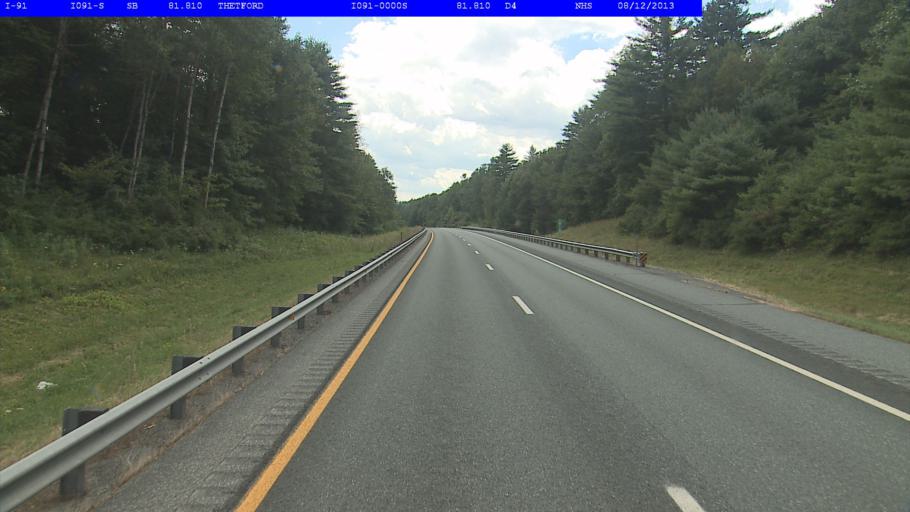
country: US
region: New Hampshire
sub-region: Grafton County
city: Lyme
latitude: 43.7803
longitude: -72.2212
